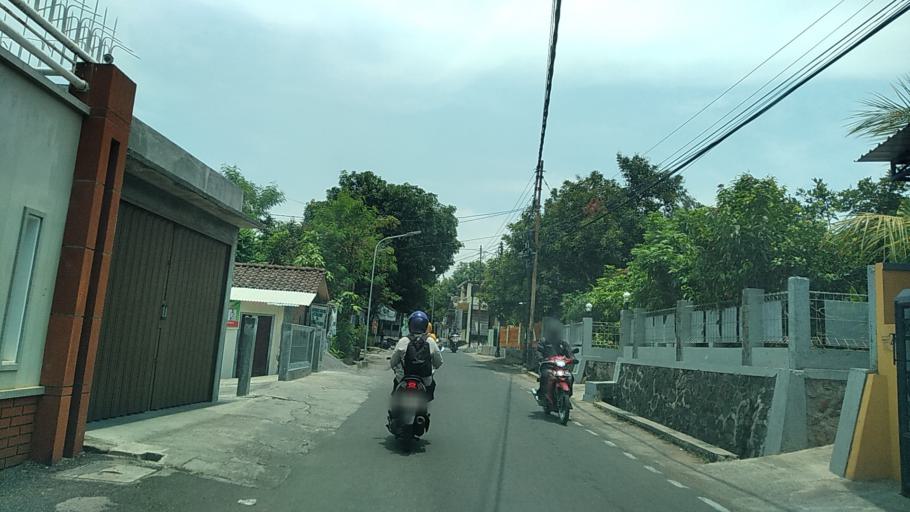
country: ID
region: Central Java
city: Semarang
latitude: -7.0628
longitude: 110.4115
